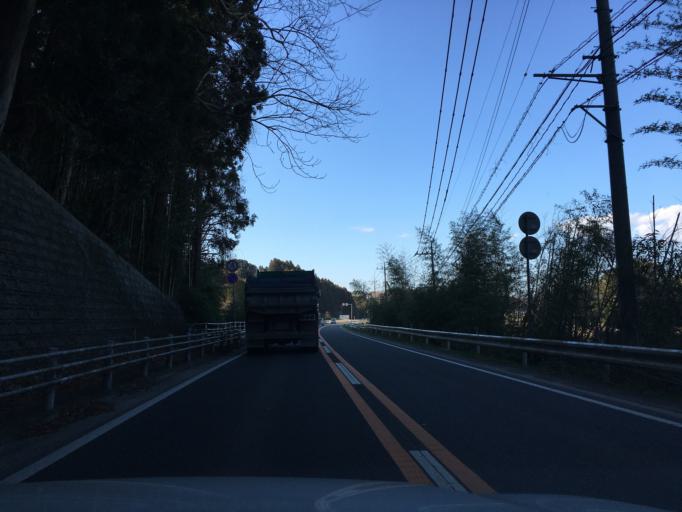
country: JP
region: Ibaraki
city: Omiya
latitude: 36.6051
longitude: 140.3993
